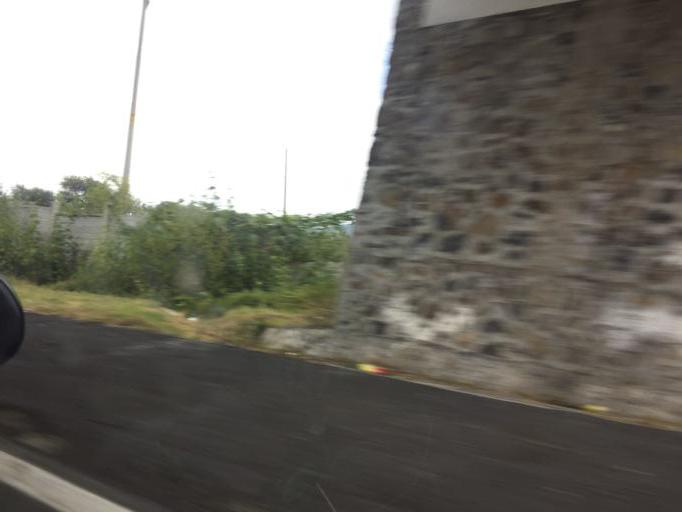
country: MX
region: Jalisco
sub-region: Ocotlan
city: Joconoxtle (La Tuna)
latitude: 20.3820
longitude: -102.7021
